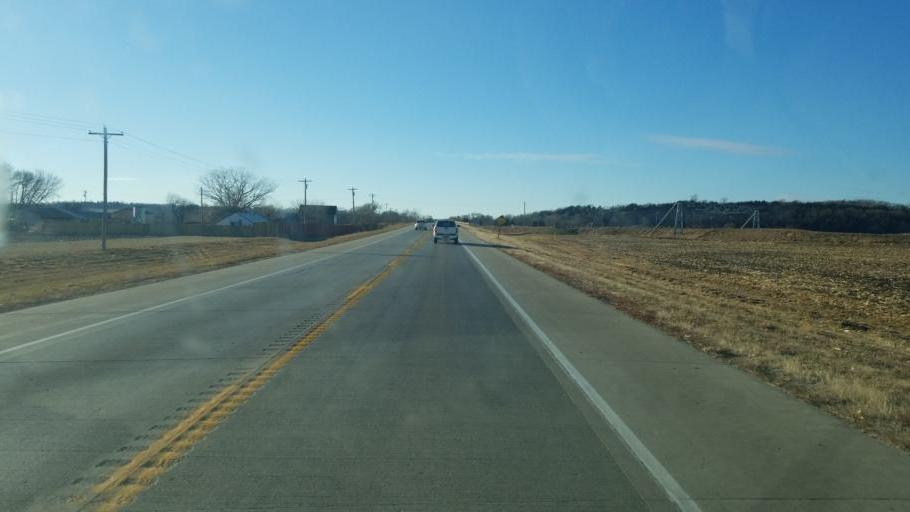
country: US
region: South Dakota
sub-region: Union County
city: Dakota Dunes
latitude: 42.4484
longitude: -96.5531
